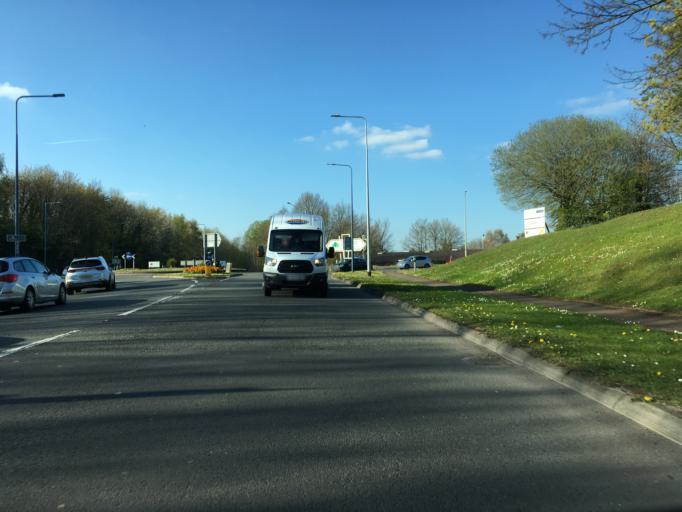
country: GB
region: Wales
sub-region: Torfaen County Borough
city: Cwmbran
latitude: 51.6342
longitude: -3.0198
